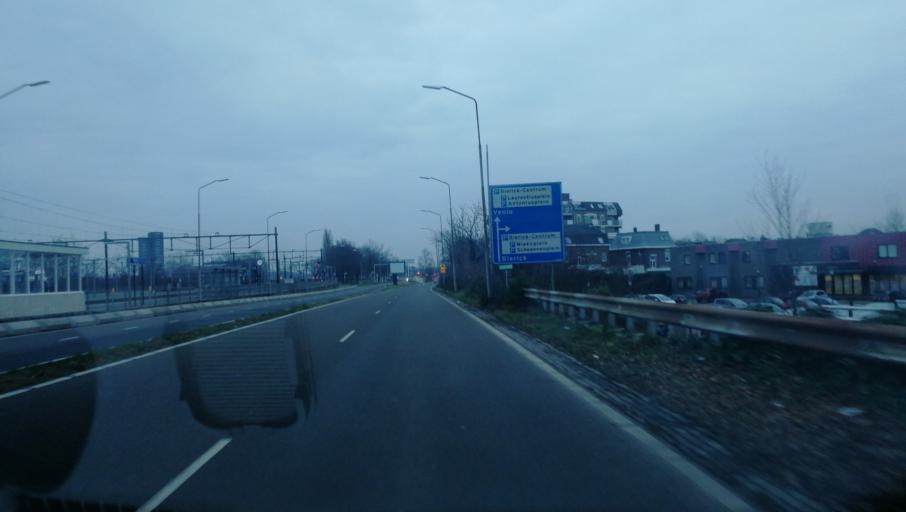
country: NL
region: Limburg
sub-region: Gemeente Venlo
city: Venlo
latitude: 51.3725
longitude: 6.1544
